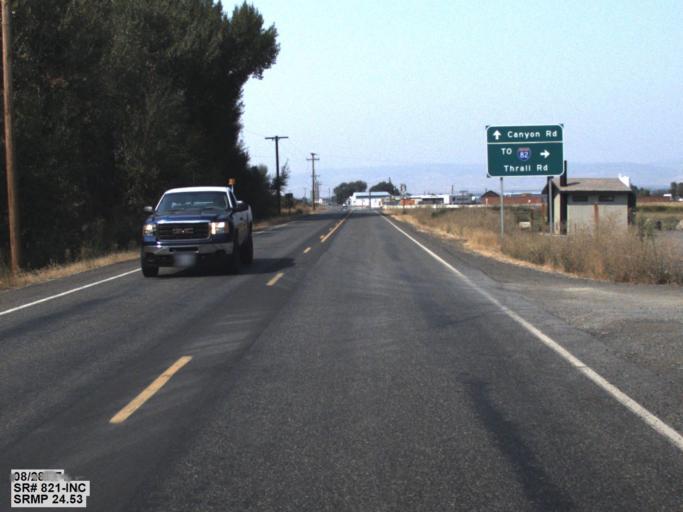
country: US
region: Washington
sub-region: Kittitas County
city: Ellensburg
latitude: 46.9246
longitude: -120.5097
